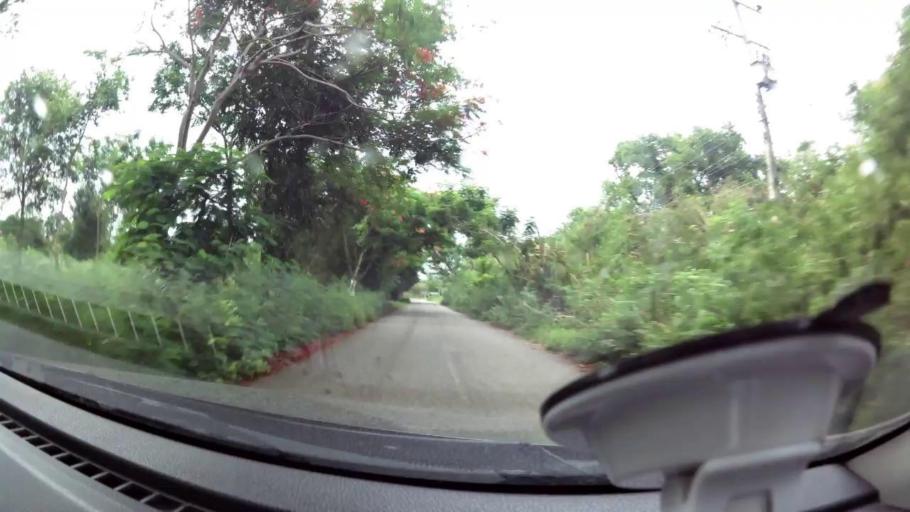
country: TH
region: Prachuap Khiri Khan
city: Pran Buri
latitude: 12.4425
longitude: 99.9697
